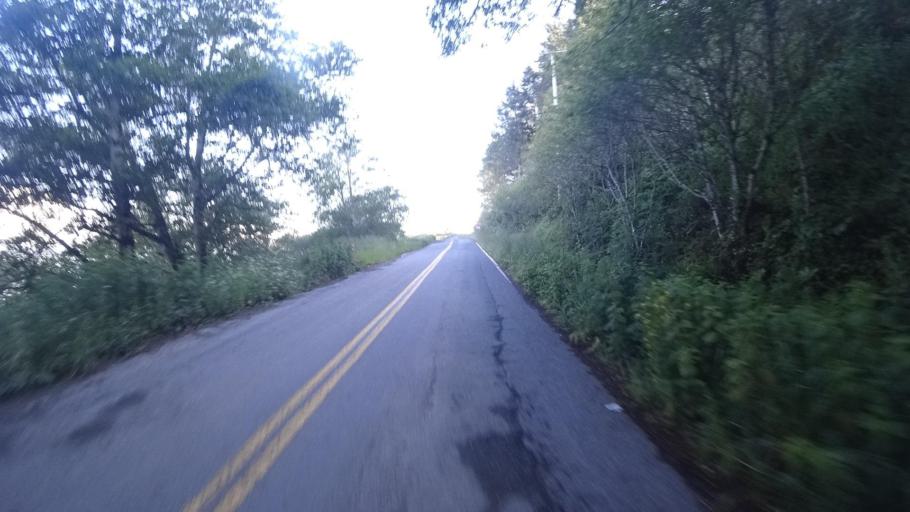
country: US
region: California
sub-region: Humboldt County
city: Westhaven-Moonstone
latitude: 41.1070
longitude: -124.1596
